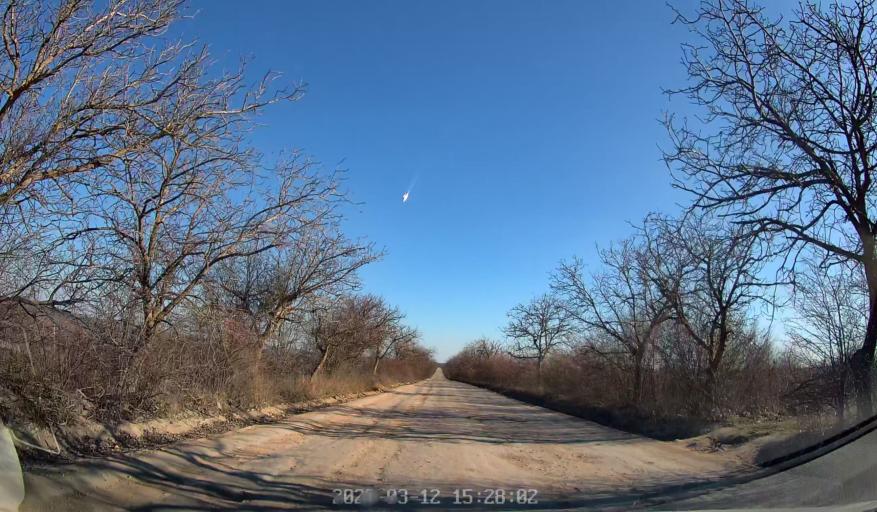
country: MD
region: Chisinau
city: Ciorescu
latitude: 47.1705
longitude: 28.9291
